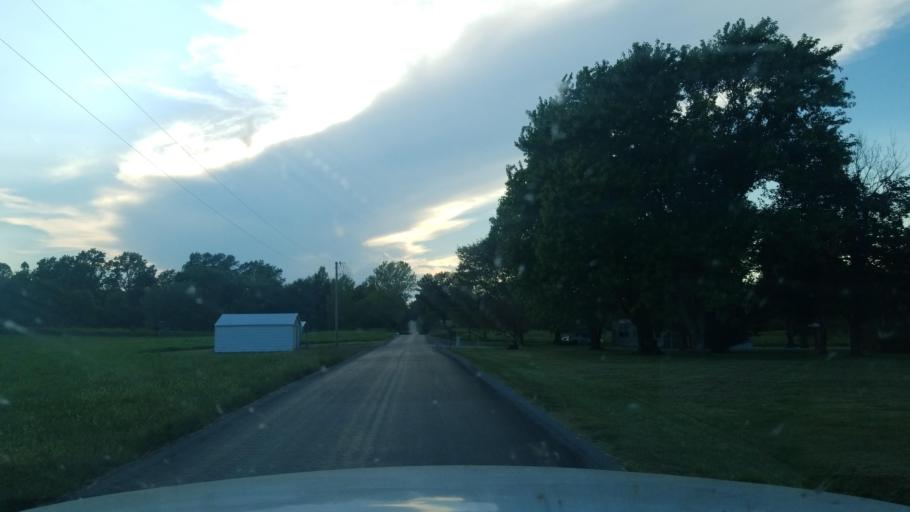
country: US
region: Illinois
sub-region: Saline County
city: Carrier Mills
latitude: 37.7906
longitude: -88.6623
